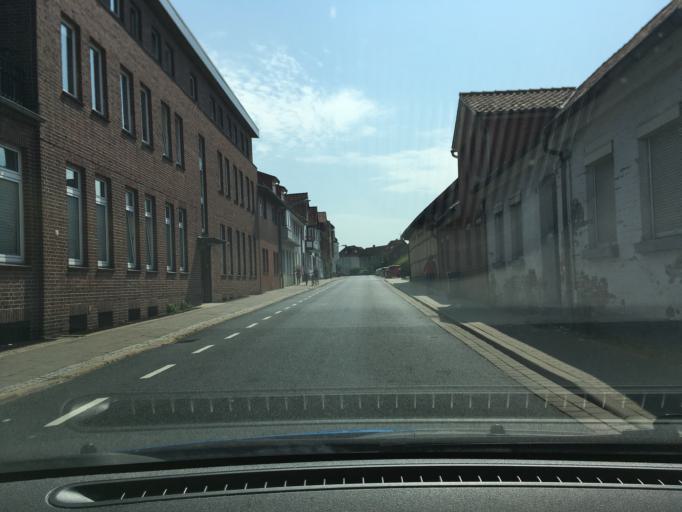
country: DE
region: Lower Saxony
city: Uelzen
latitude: 52.9639
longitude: 10.5676
